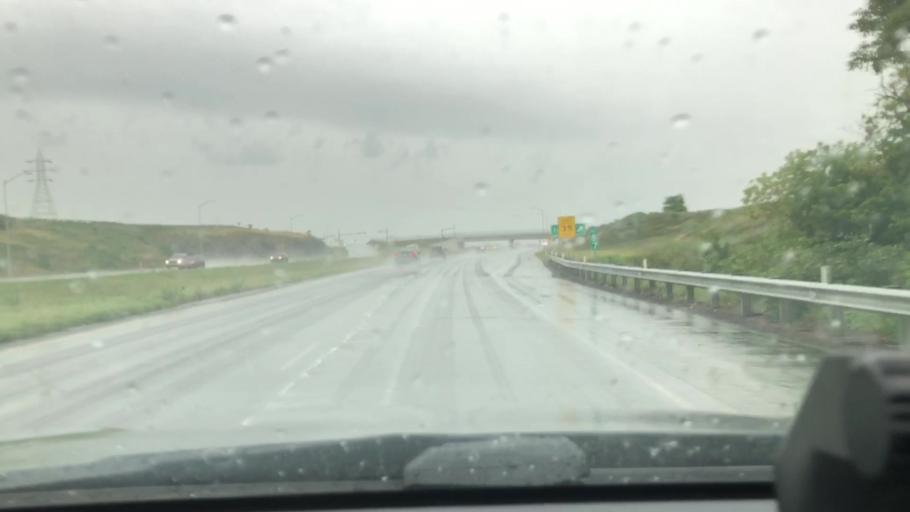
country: US
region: Pennsylvania
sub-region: Northampton County
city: Tatamy
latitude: 40.7437
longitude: -75.2652
